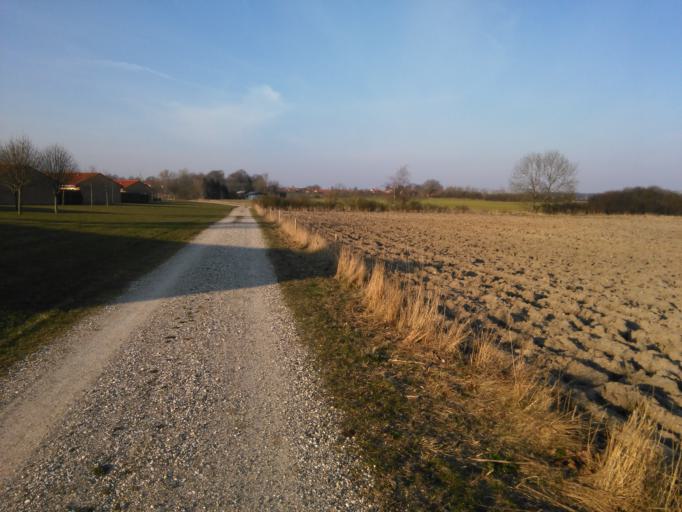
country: DK
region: Central Jutland
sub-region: Arhus Kommune
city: Beder
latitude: 56.0532
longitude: 10.2165
